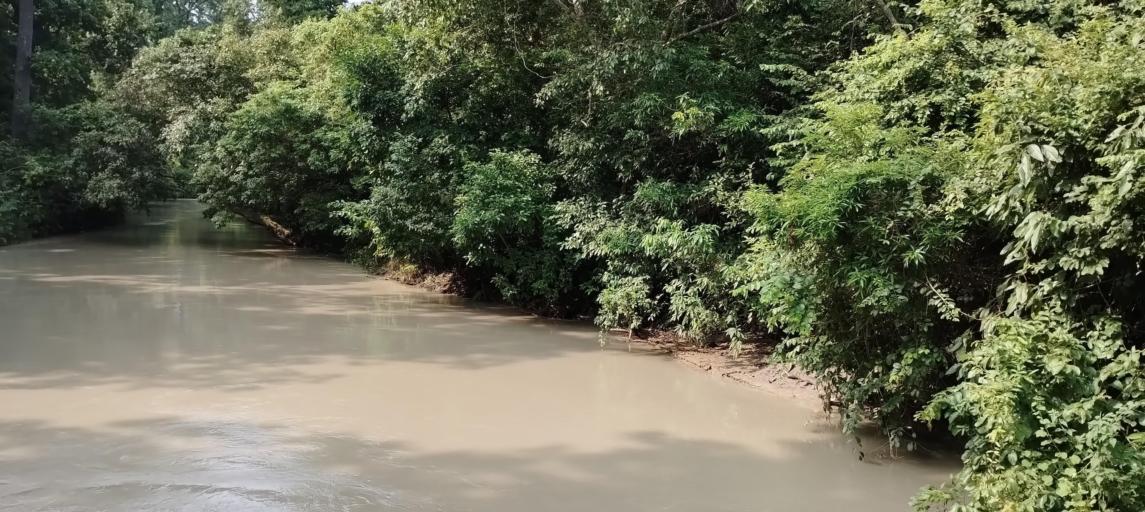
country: NP
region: Far Western
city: Tikapur
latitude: 28.4726
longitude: 81.2511
